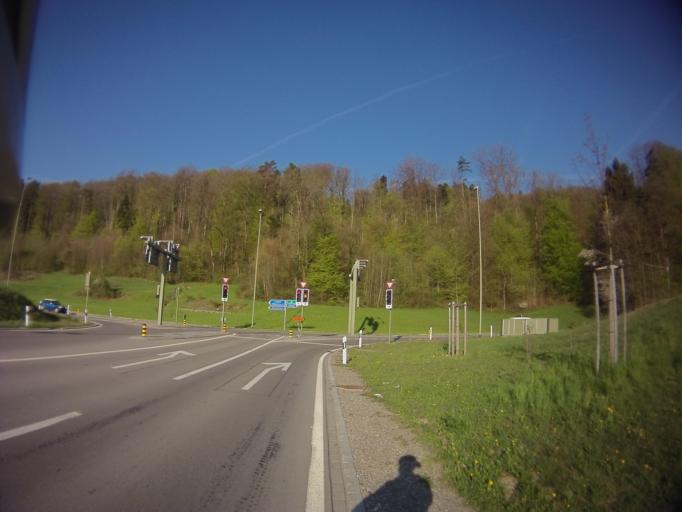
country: CH
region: Zurich
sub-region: Bezirk Affoltern
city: Wettswil / Wettswil (Dorf)
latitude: 47.3347
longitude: 8.4597
